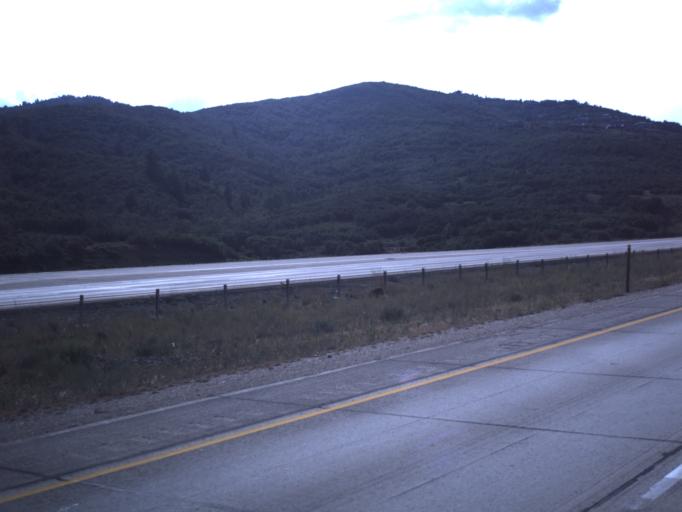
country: US
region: Utah
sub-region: Summit County
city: Park City
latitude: 40.6288
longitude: -111.4442
